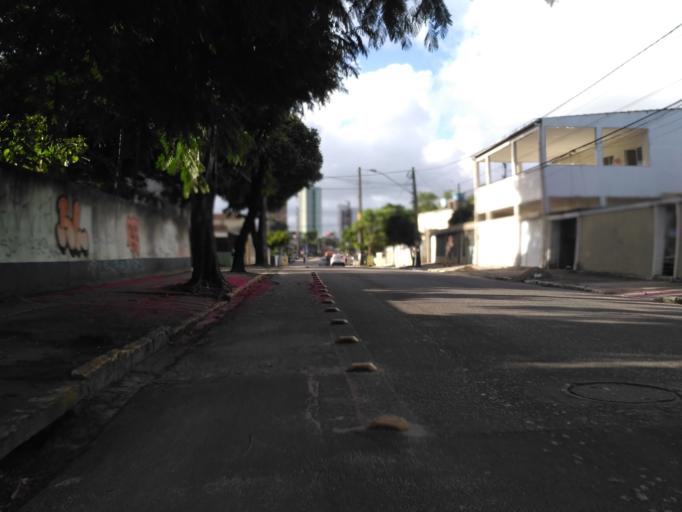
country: BR
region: Pernambuco
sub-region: Recife
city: Recife
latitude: -8.0487
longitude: -34.9409
